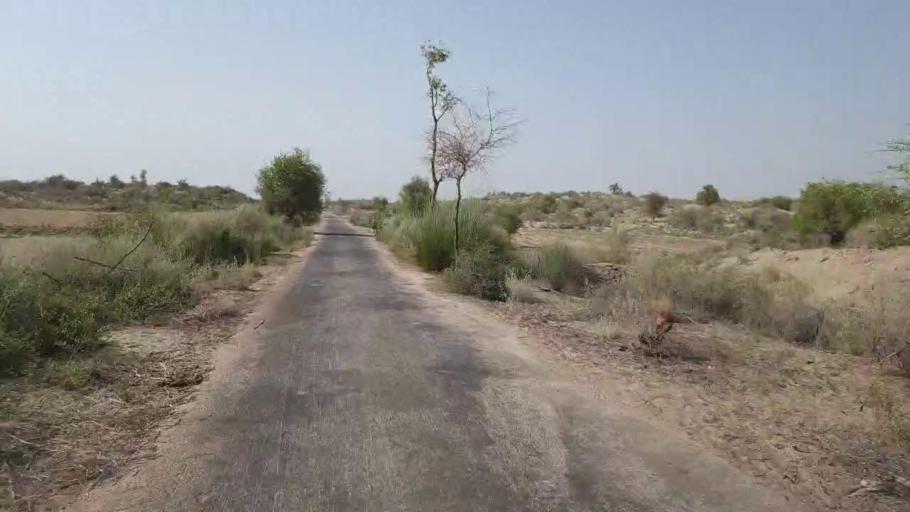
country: PK
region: Sindh
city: Jam Sahib
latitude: 26.5674
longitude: 68.9225
